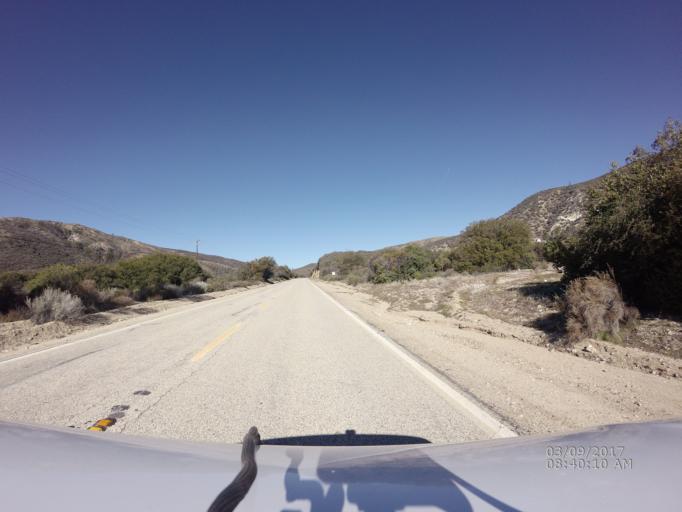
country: US
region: California
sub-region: Los Angeles County
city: Green Valley
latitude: 34.6854
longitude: -118.4674
